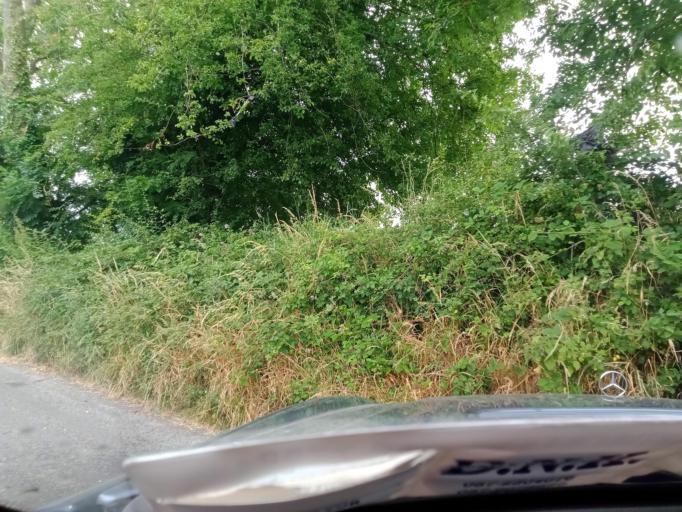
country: IE
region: Leinster
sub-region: Kilkenny
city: Mooncoin
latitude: 52.2855
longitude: -7.1910
